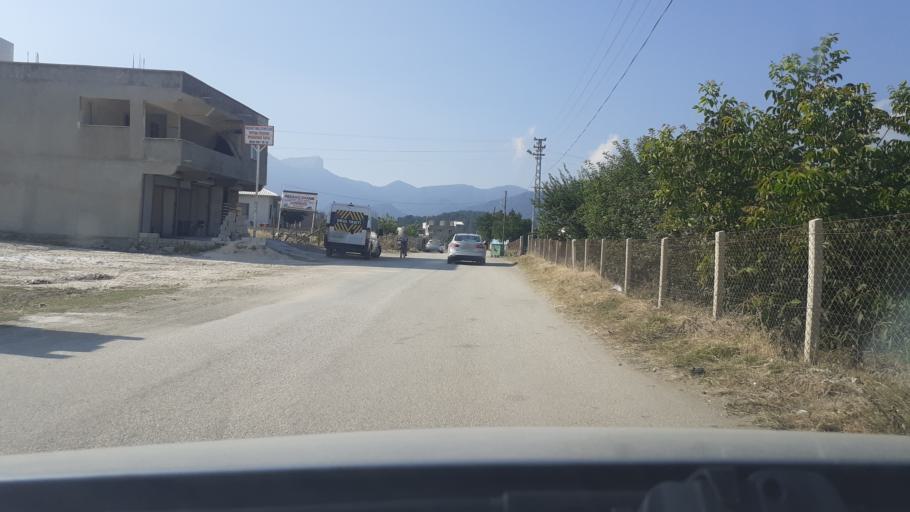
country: TR
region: Hatay
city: Gyuvench
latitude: 36.6205
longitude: 36.3438
